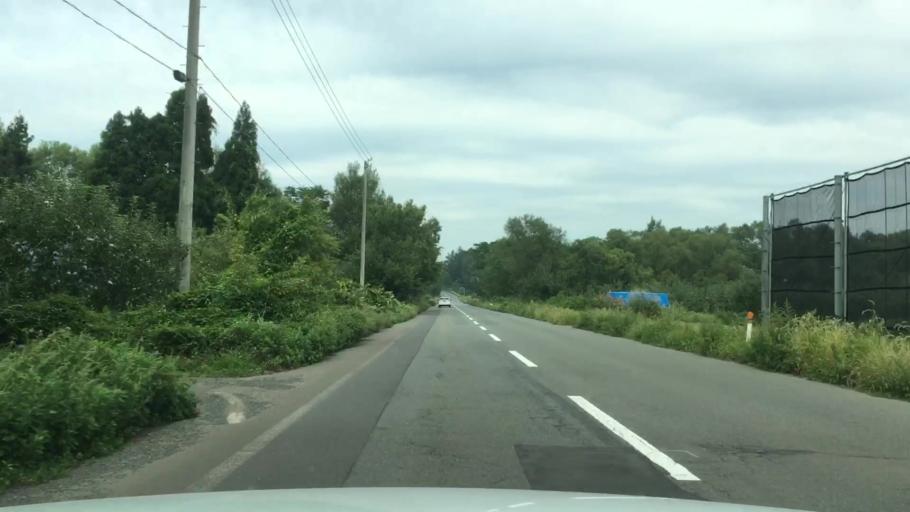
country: JP
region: Aomori
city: Shimokizukuri
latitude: 40.6816
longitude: 140.3709
